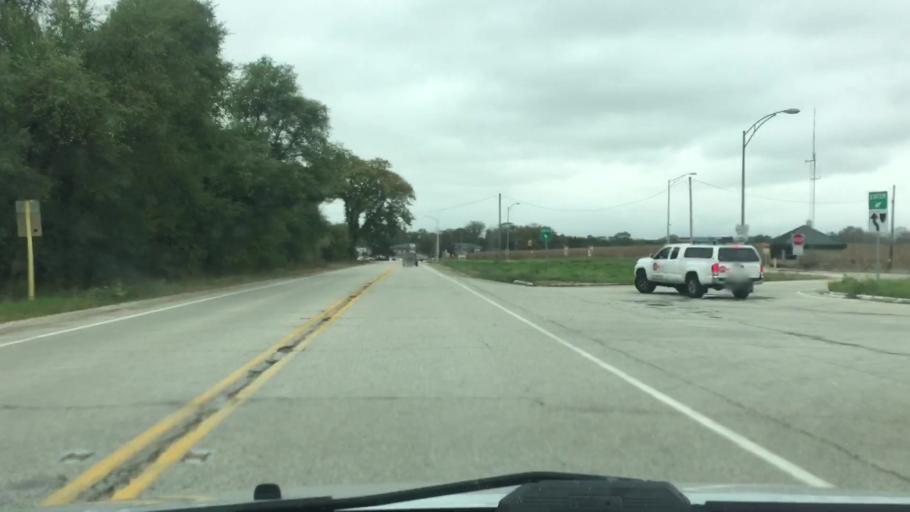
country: US
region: Illinois
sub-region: McHenry County
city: Richmond
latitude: 42.4924
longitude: -88.3092
